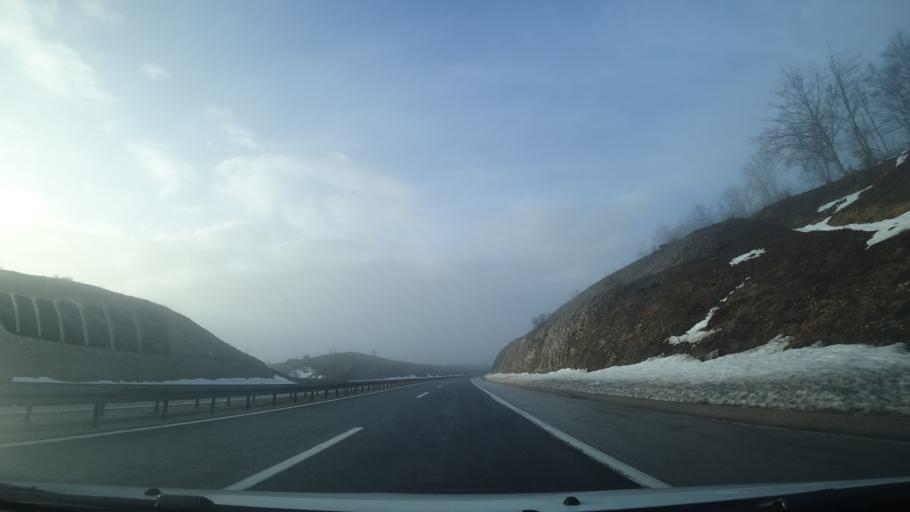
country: HR
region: Licko-Senjska
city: Brinje
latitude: 45.0427
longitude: 15.1777
